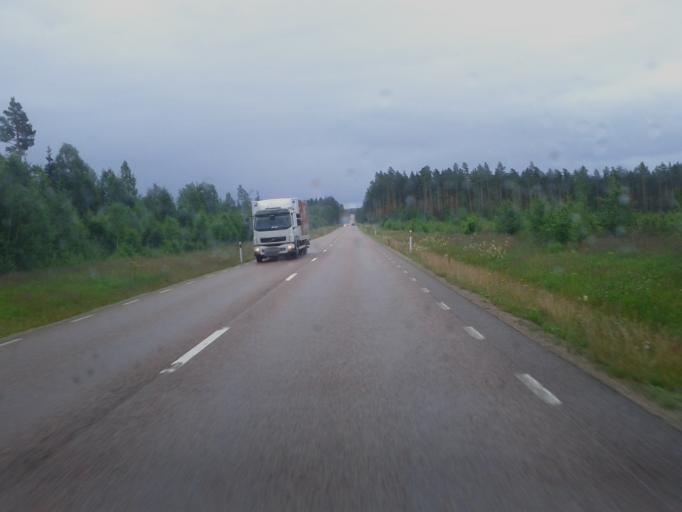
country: SE
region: Dalarna
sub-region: Leksand Municipality
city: Siljansnas
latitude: 60.9299
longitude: 14.7933
